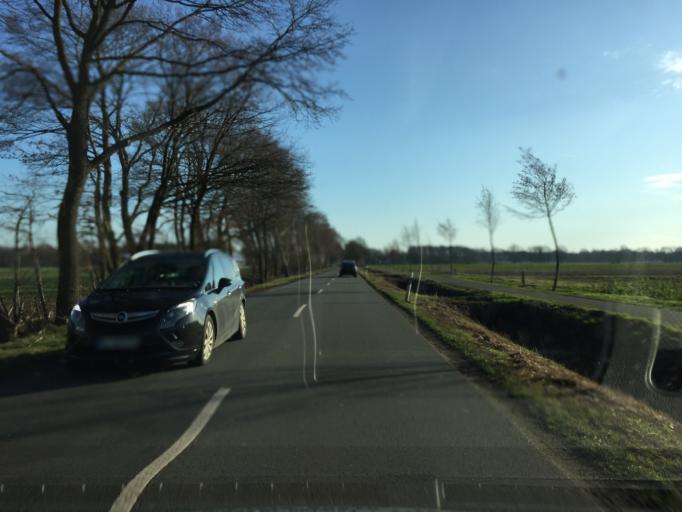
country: DE
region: Lower Saxony
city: Estorf
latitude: 52.5518
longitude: 9.1911
